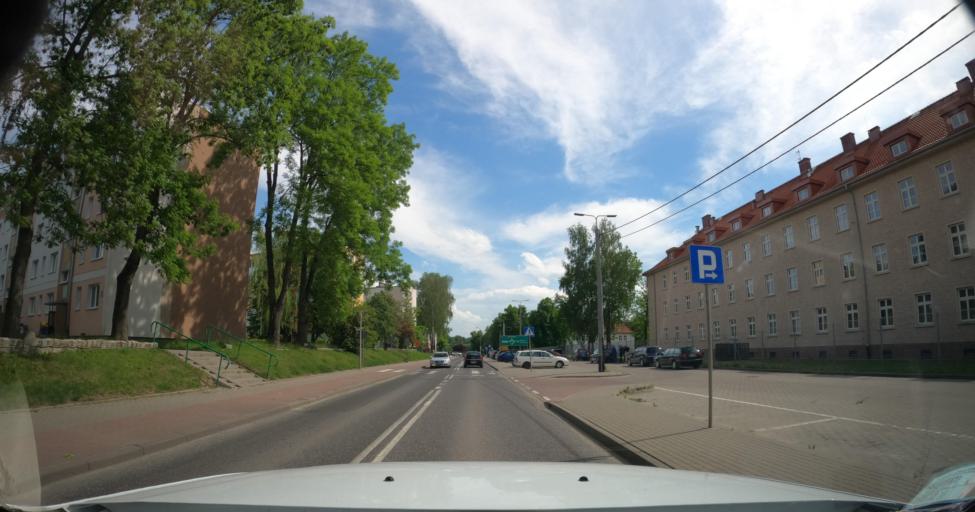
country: PL
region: Warmian-Masurian Voivodeship
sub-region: Powiat lidzbarski
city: Lidzbark Warminski
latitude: 54.1287
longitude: 20.5657
